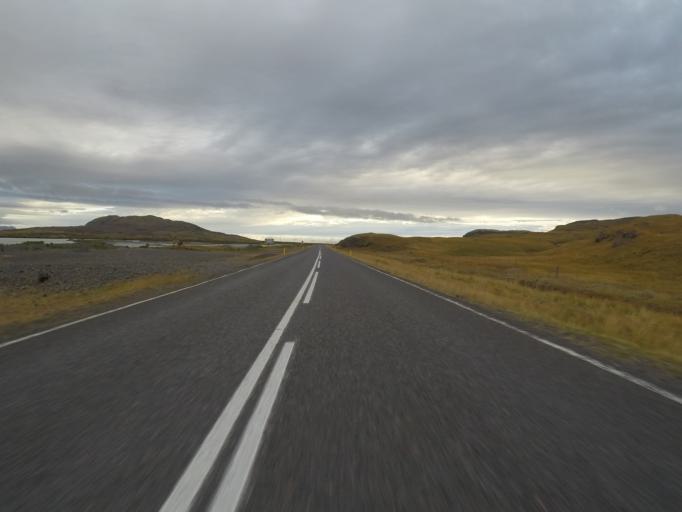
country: IS
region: South
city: Vestmannaeyjar
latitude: 64.0630
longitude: -20.1148
